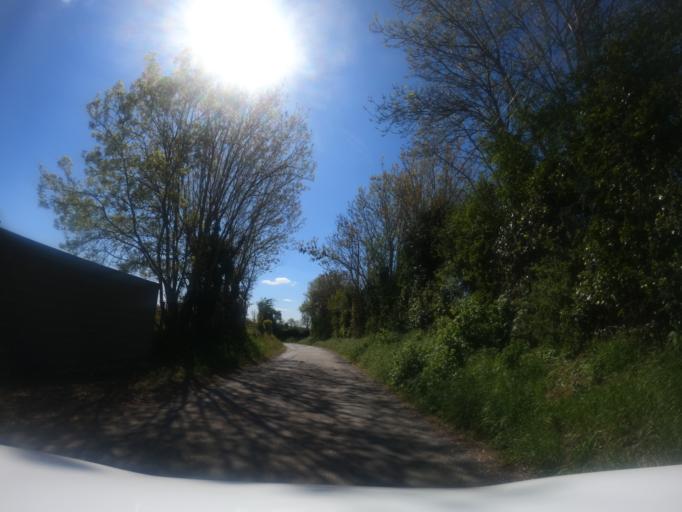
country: FR
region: Pays de la Loire
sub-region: Departement de la Vendee
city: Fontenay-le-Comte
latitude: 46.4417
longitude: -0.8723
